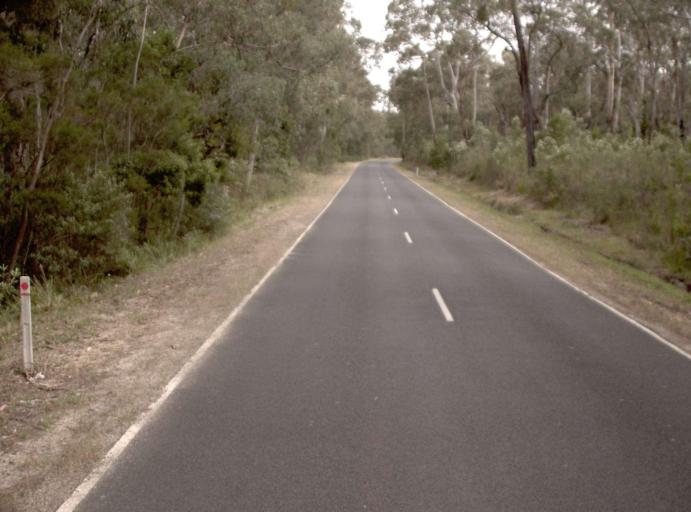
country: AU
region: Victoria
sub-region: Latrobe
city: Traralgon
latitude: -38.4389
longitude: 146.8234
